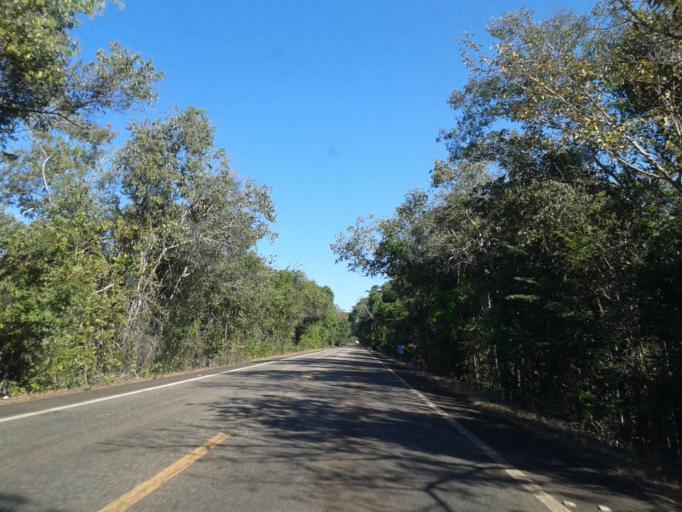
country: BR
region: Goias
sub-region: Crixas
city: Crixas
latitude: -14.0107
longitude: -50.3257
